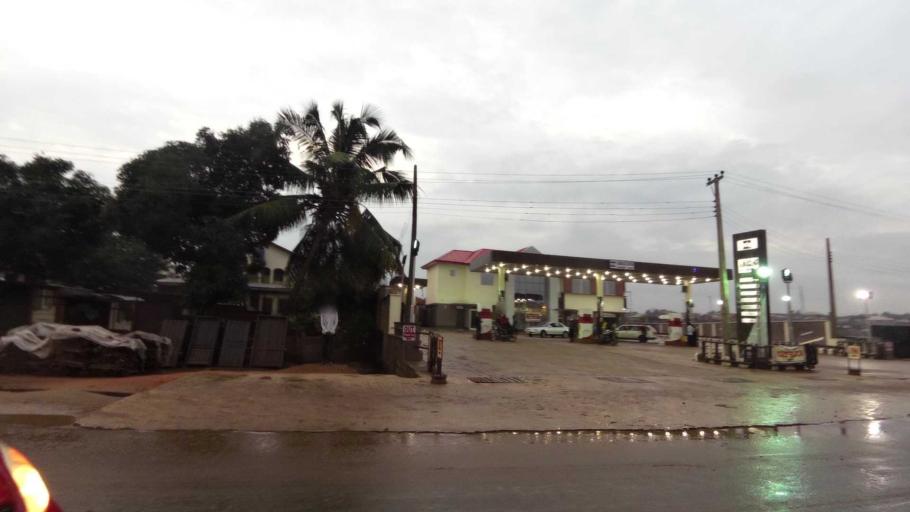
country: NG
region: Oyo
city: Ibadan
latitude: 7.4346
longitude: 3.9442
